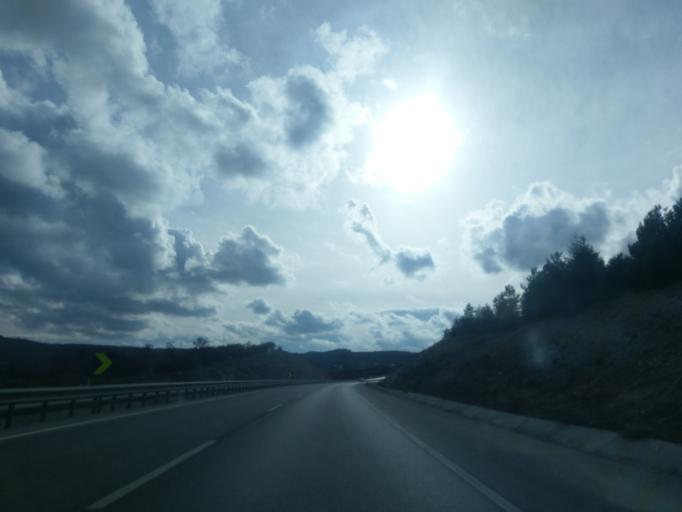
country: TR
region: Kuetahya
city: Sabuncu
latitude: 39.5960
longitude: 30.1440
